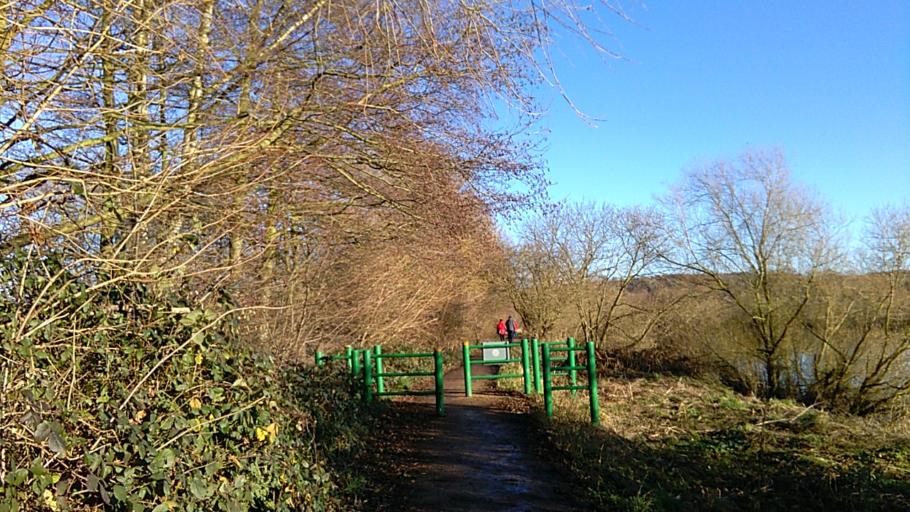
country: GB
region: England
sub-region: Nottinghamshire
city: Gotham
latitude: 52.9039
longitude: -1.2181
